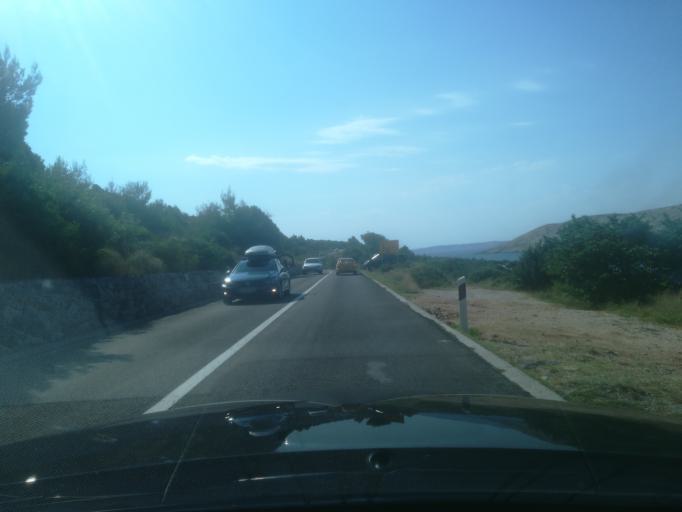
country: HR
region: Primorsko-Goranska
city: Banjol
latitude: 44.7120
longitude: 14.8290
